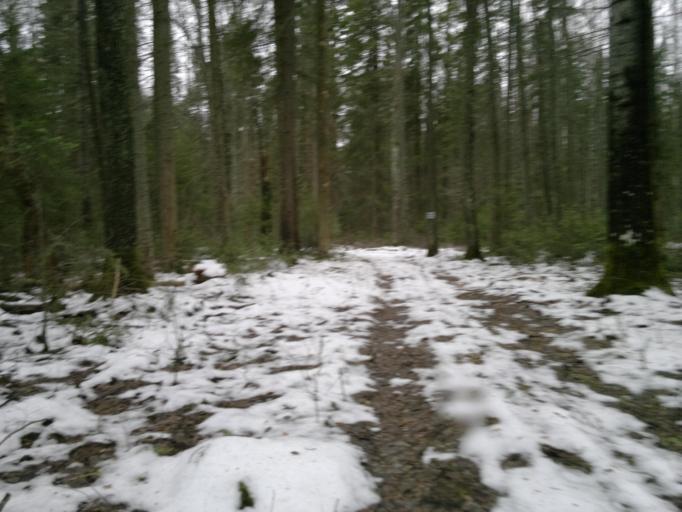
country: RU
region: Mariy-El
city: Yoshkar-Ola
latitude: 56.5938
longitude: 47.9682
